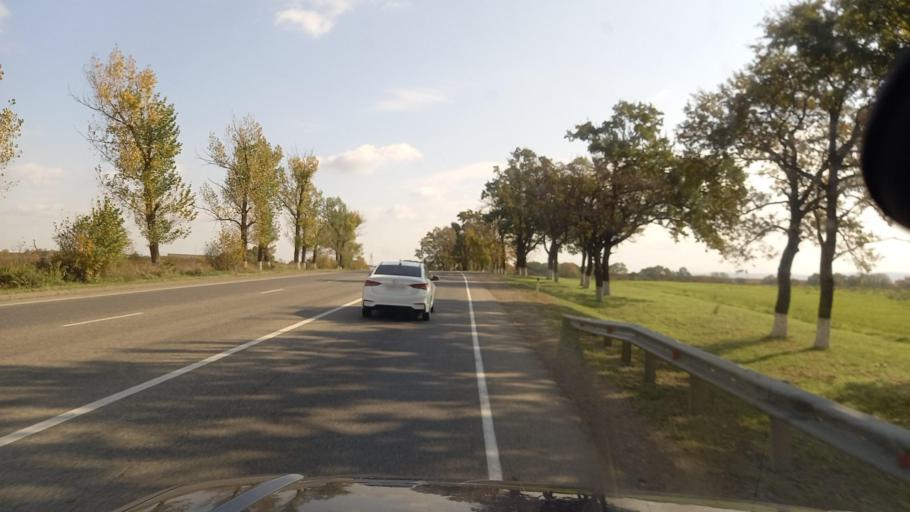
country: RU
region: Krasnodarskiy
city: Akhtyrskiy
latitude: 44.8543
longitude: 38.3404
